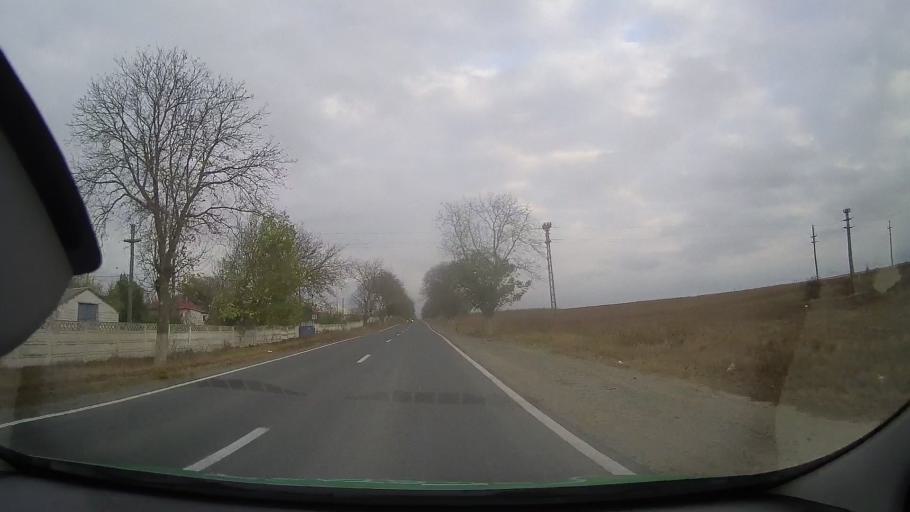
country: RO
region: Constanta
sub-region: Comuna Adamclisi
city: Adamclisi
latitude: 44.0885
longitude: 27.9662
